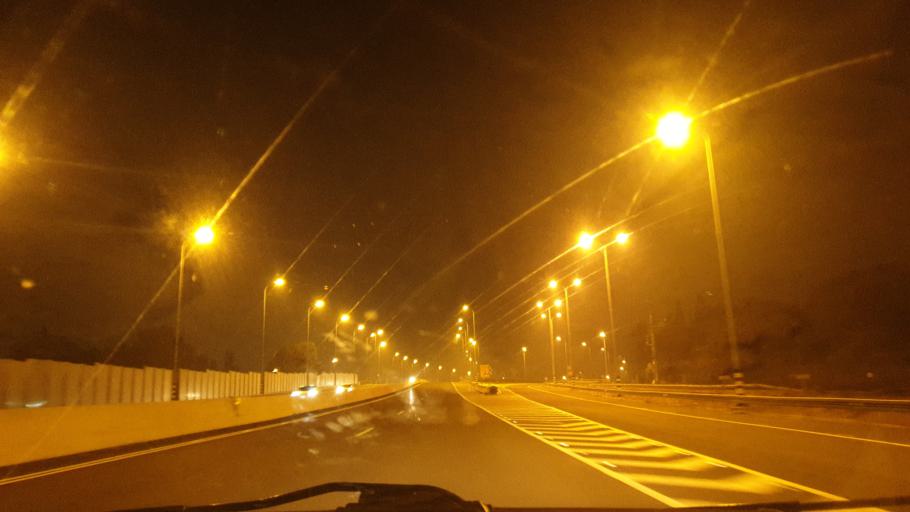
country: IL
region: Central District
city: Ramla
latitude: 31.9455
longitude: 34.8607
